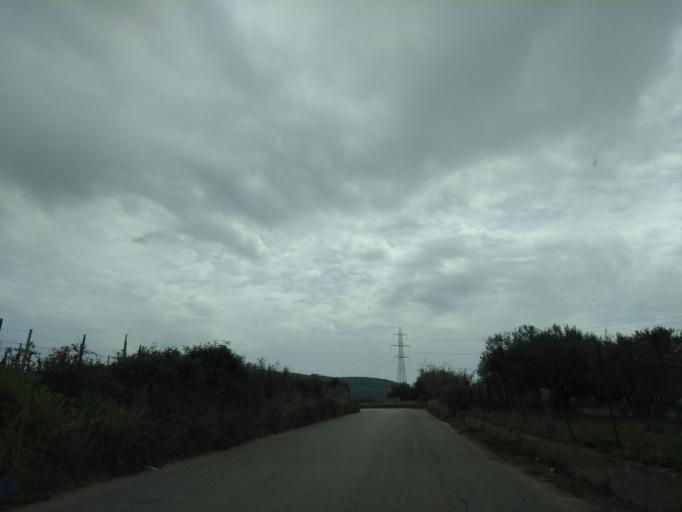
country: IT
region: Sicily
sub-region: Palermo
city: Partinico
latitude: 37.9947
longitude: 13.0657
